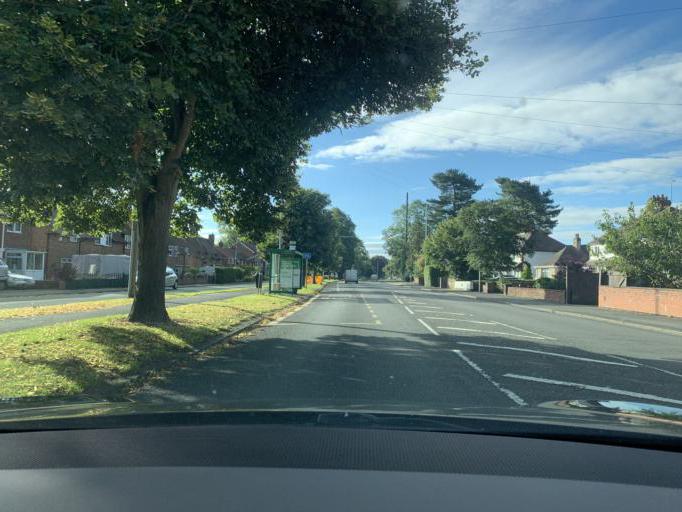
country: GB
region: England
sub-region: Staffordshire
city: Stafford
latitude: 52.8229
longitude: -2.1385
